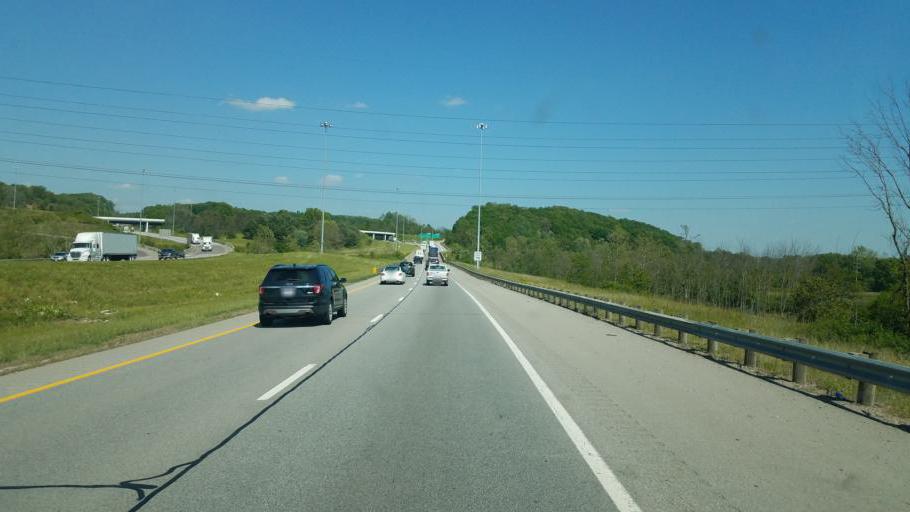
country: US
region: Ohio
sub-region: Guernsey County
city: Cambridge
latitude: 39.9966
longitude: -81.5676
